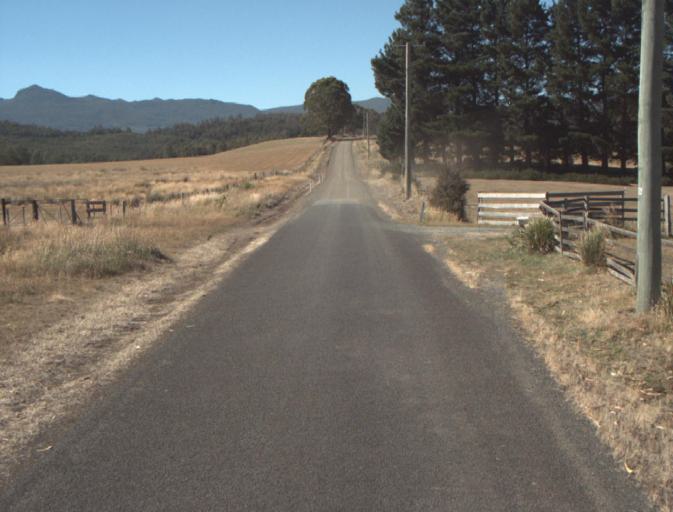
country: AU
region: Tasmania
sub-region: Launceston
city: Newstead
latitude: -41.3083
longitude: 147.3190
